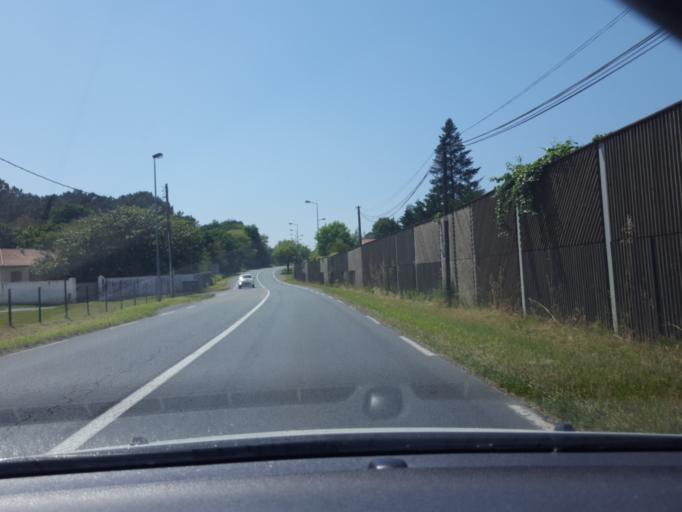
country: FR
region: Aquitaine
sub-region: Departement des Landes
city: Tarnos
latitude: 43.5525
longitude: -1.4634
